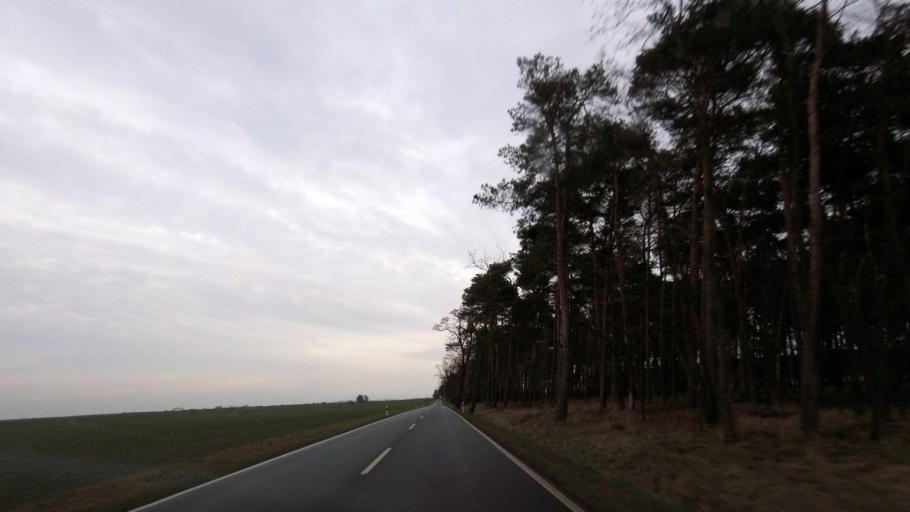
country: DE
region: Brandenburg
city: Niedergorsdorf
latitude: 51.9326
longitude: 12.9692
